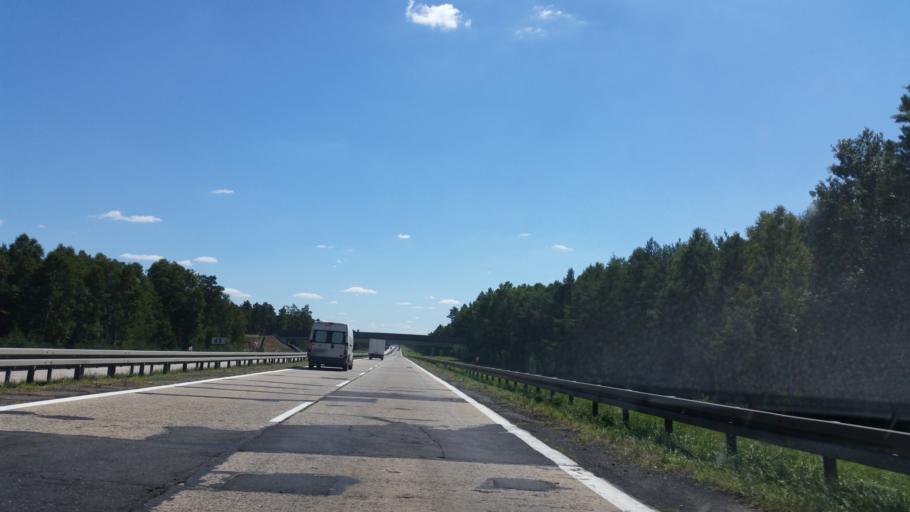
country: PL
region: Lower Silesian Voivodeship
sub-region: Powiat boleslawiecki
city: Boleslawiec
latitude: 51.3928
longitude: 15.5318
